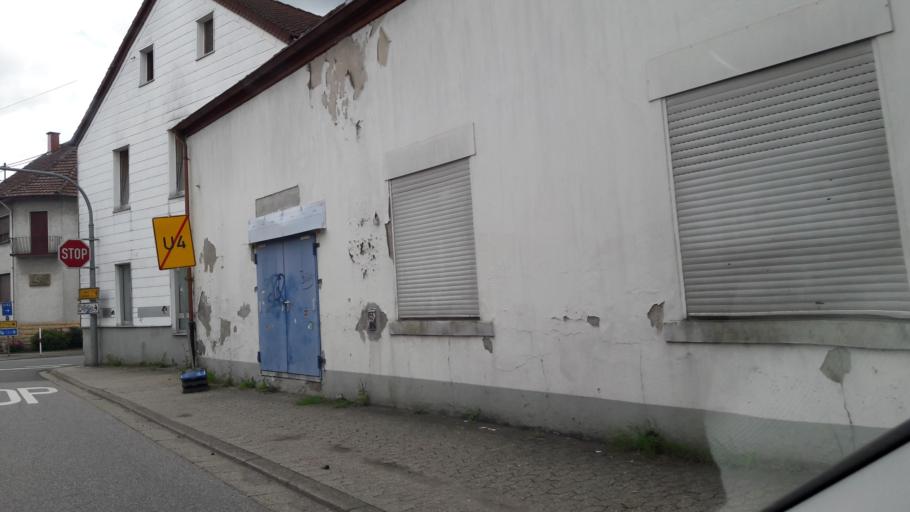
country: DE
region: Saarland
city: Tholey
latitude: 49.4649
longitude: 7.0003
